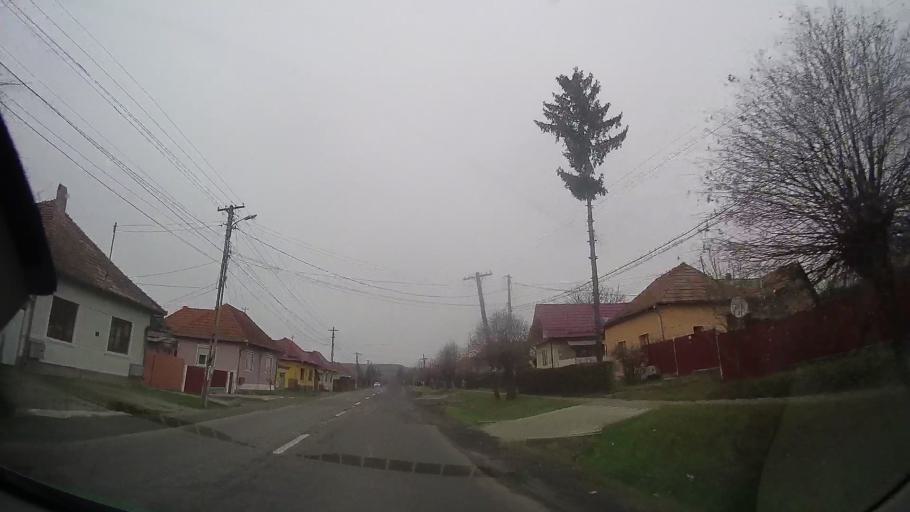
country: RO
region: Mures
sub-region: Comuna Ceausu de Campie
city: Ceausu de Campie
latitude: 46.6433
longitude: 24.5042
